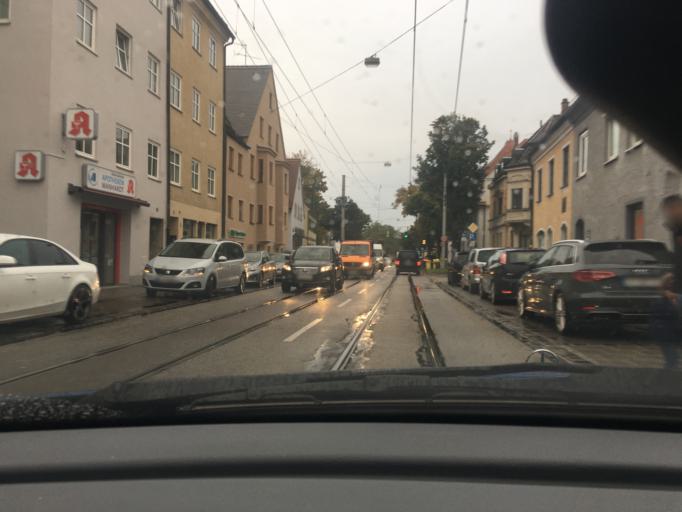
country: DE
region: Bavaria
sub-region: Swabia
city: Stadtbergen
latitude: 48.3798
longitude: 10.8530
